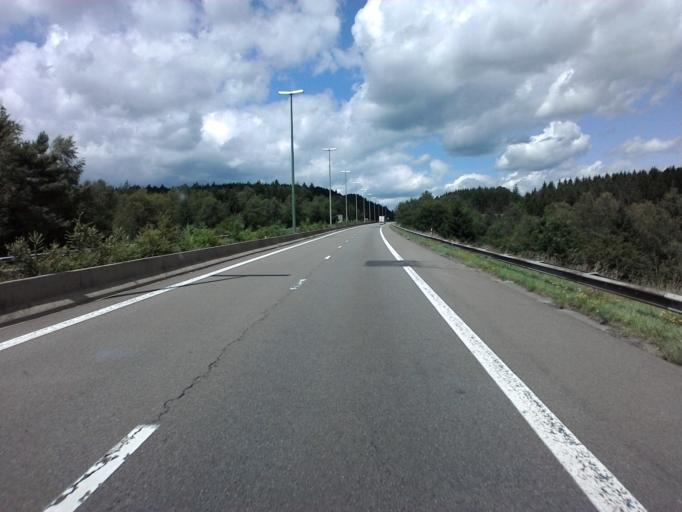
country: BE
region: Wallonia
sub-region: Province du Luxembourg
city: Manhay
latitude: 50.3164
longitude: 5.7072
